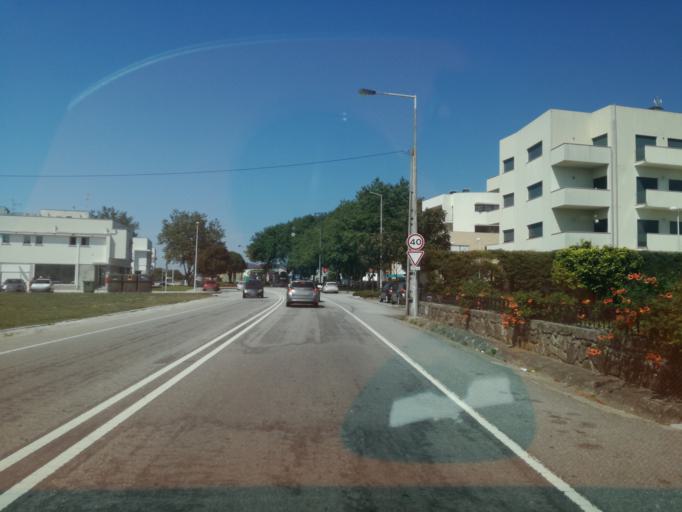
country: PT
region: Braga
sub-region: Esposende
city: Esposende
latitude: 41.5301
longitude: -8.7759
